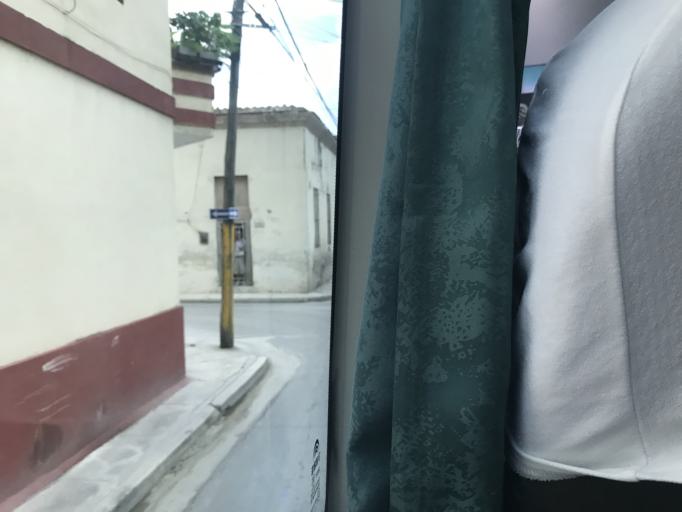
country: CU
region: Holguin
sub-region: Municipio de Holguin
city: Holguin
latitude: 20.8894
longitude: -76.2591
